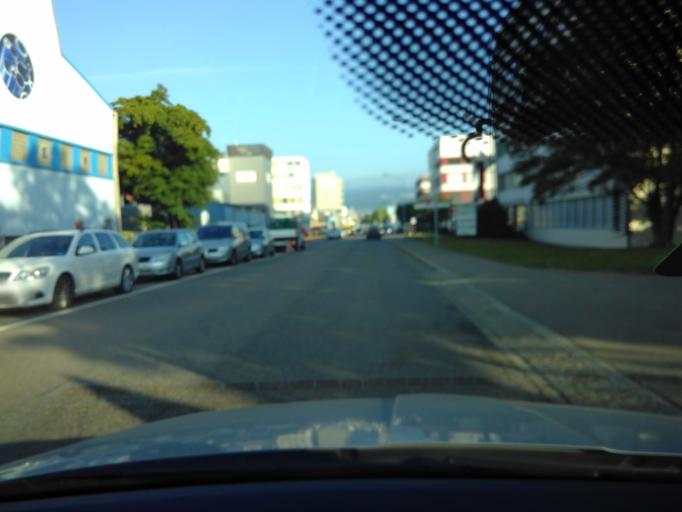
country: CH
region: Zurich
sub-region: Bezirk Dielsdorf
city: Regensdorf / Feldblumen-Riedthofstrasse
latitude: 47.4399
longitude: 8.4682
